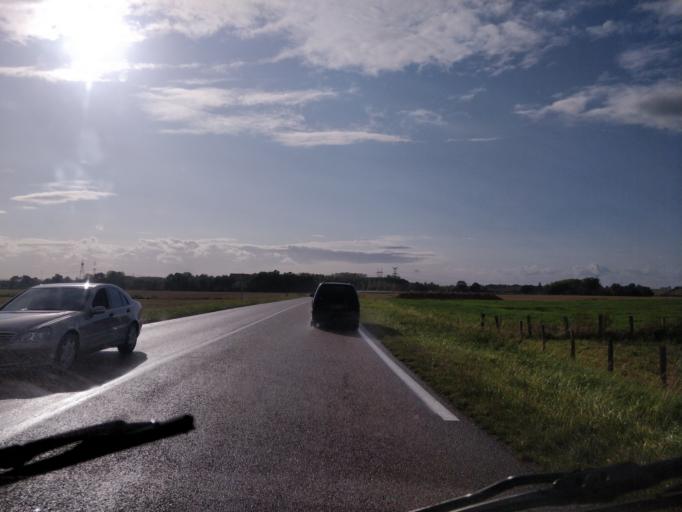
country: FR
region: Champagne-Ardenne
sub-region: Departement de l'Aube
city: Lusigny-sur-Barse
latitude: 48.2621
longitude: 4.2301
